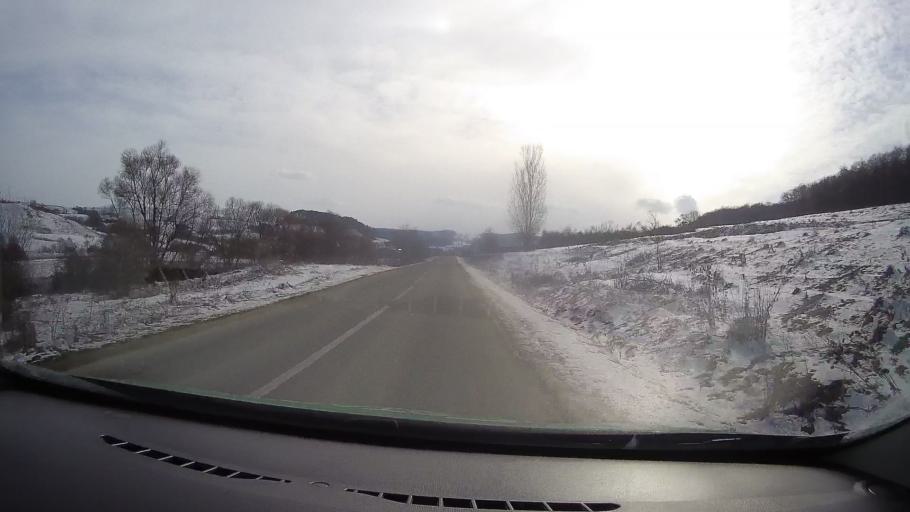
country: RO
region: Sibiu
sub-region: Comuna Bradeni
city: Bradeni
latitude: 46.0906
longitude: 24.8338
